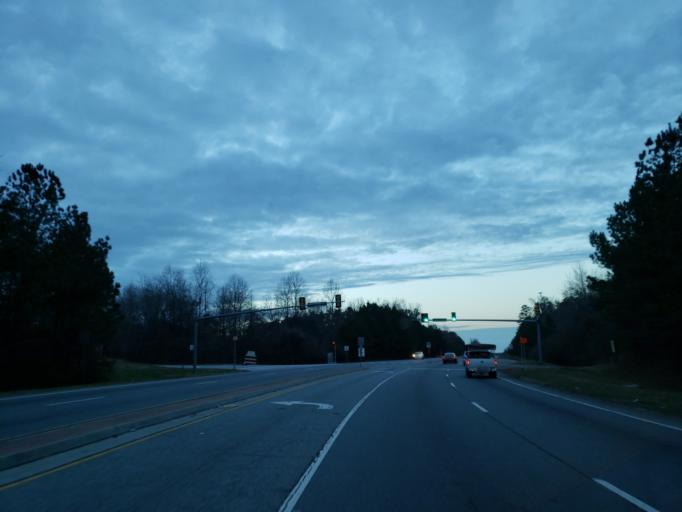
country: US
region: Georgia
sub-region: Cobb County
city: Powder Springs
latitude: 33.8706
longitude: -84.6342
